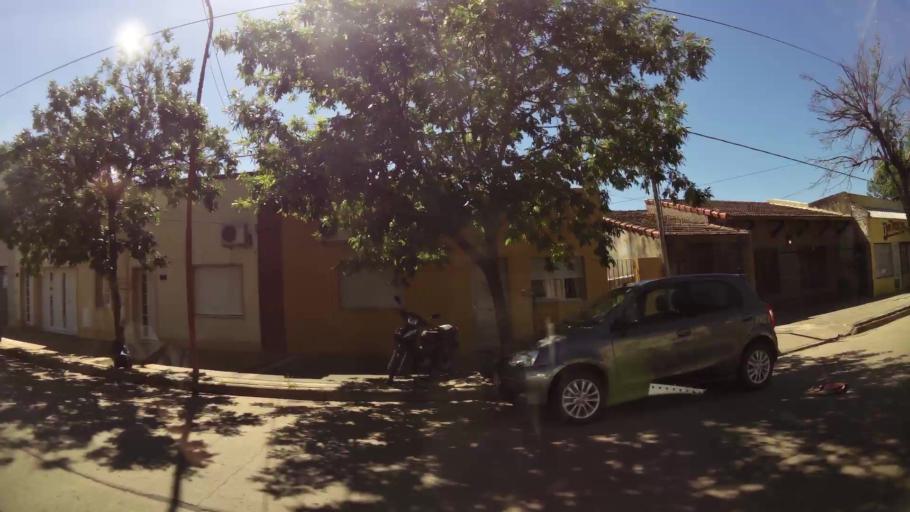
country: AR
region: Santa Fe
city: Esperanza
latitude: -31.4420
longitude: -60.9272
